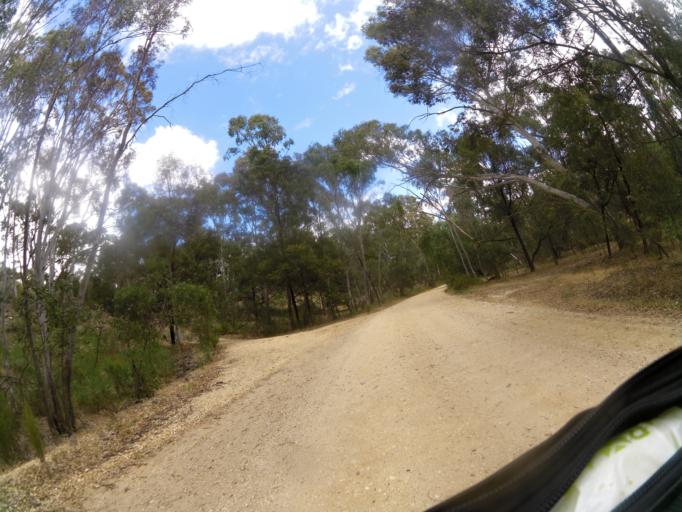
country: AU
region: Victoria
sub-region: Mount Alexander
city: Castlemaine
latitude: -37.0314
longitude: 144.2573
